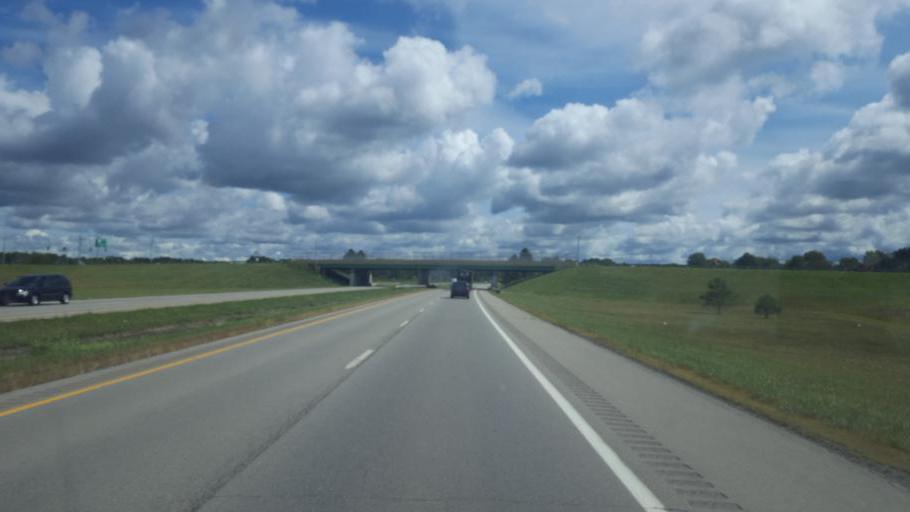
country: US
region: Ohio
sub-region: Lorain County
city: Elyria
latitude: 41.3173
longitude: -82.1194
